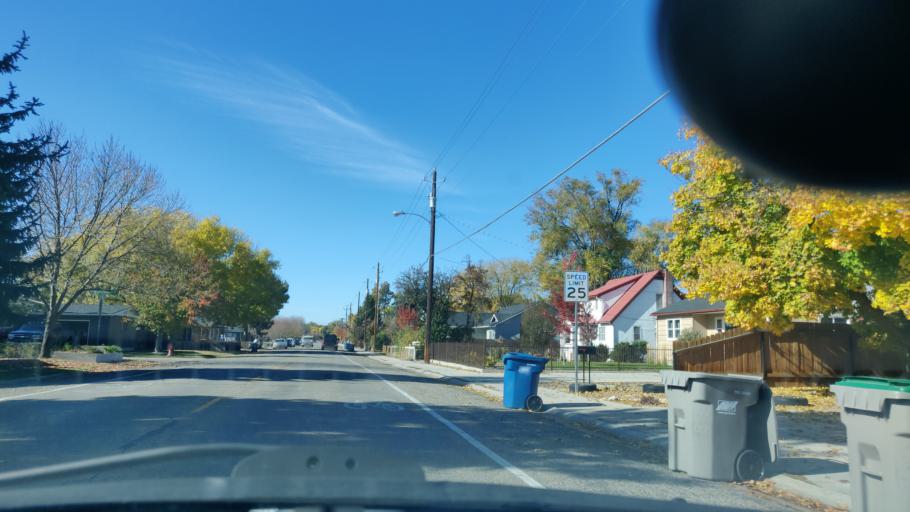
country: US
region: Idaho
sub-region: Ada County
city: Garden City
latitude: 43.5934
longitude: -116.2388
